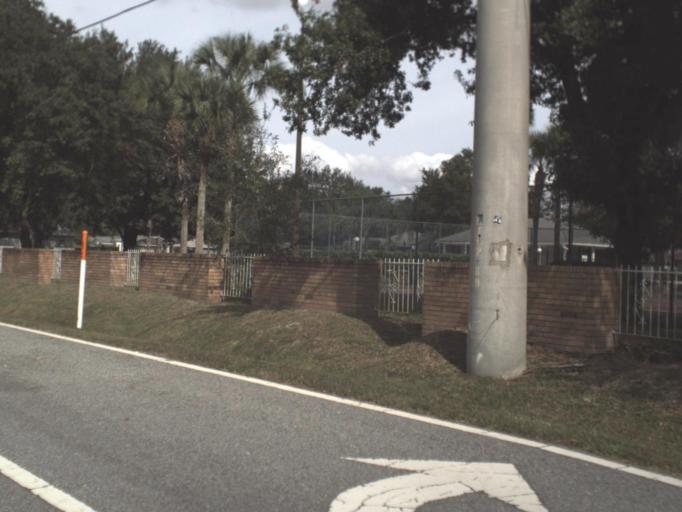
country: US
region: Florida
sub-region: Osceola County
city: Campbell
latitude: 28.2098
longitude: -81.4761
